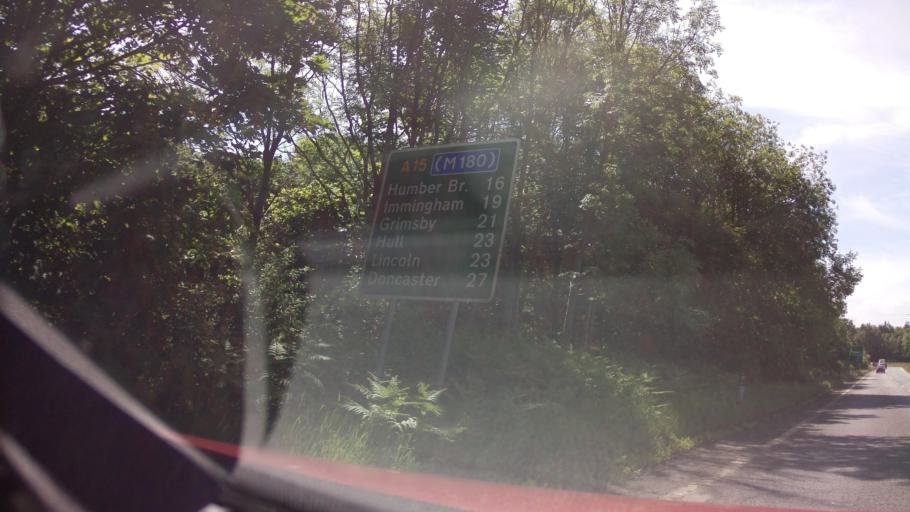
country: GB
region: England
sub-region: North Lincolnshire
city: Scawby
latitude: 53.5475
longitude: -0.5572
